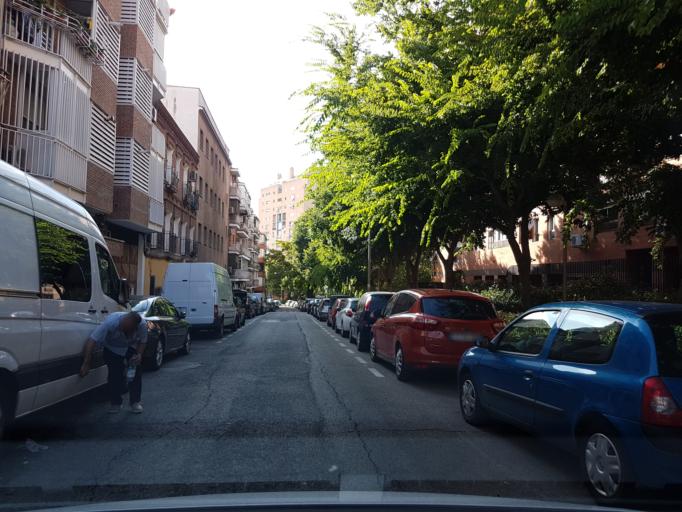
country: ES
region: Madrid
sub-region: Provincia de Madrid
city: Puente de Vallecas
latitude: 40.4049
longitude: -3.6600
